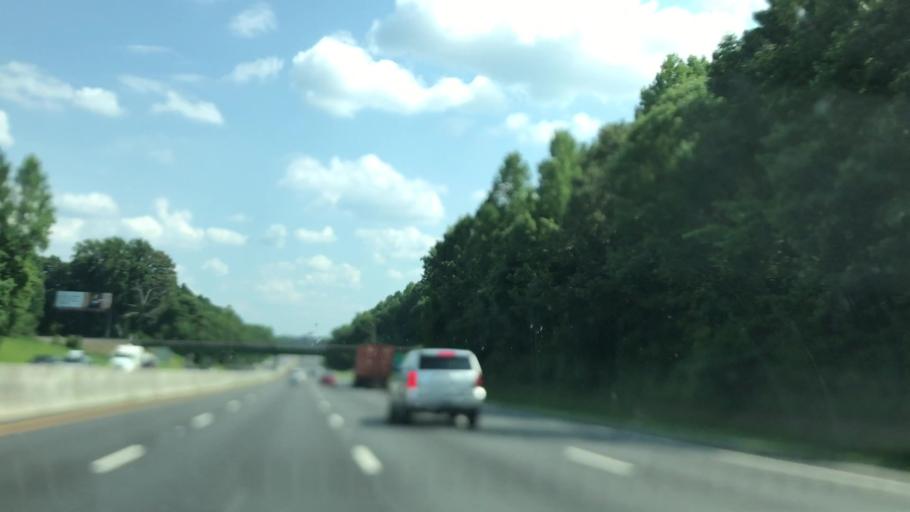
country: US
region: South Carolina
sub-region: York County
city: Rock Hill
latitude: 34.9525
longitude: -80.9777
